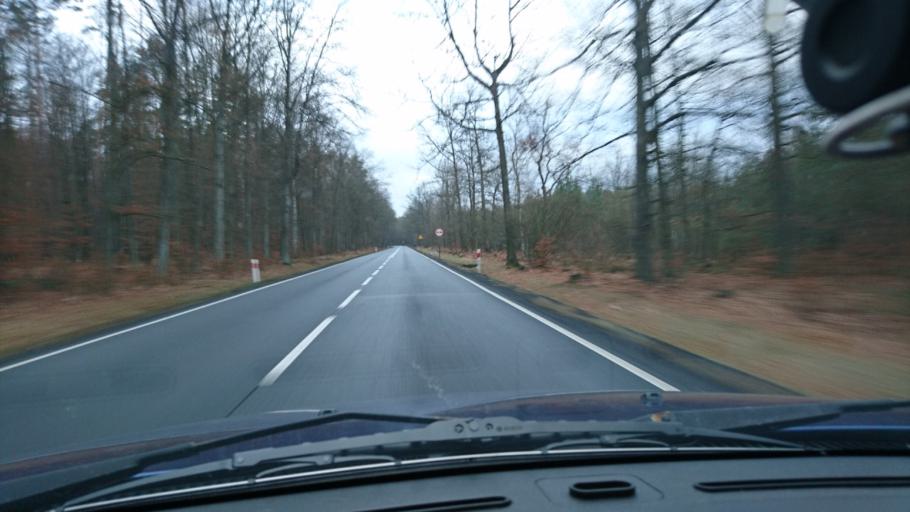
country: PL
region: Opole Voivodeship
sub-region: Powiat oleski
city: Olesno
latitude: 50.9335
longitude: 18.3321
